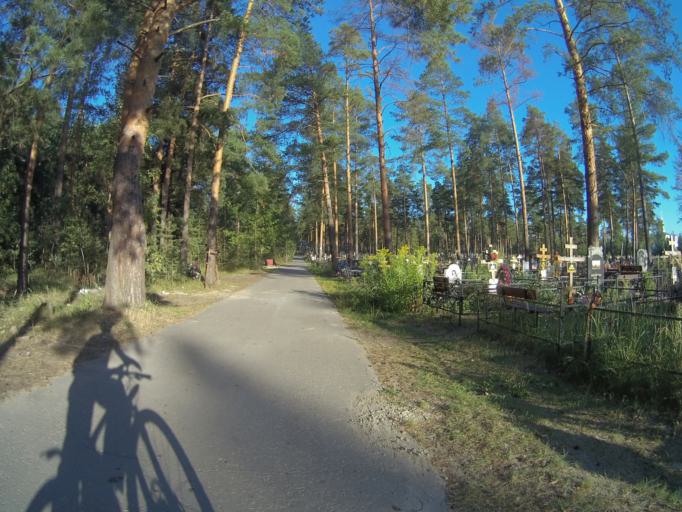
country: RU
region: Vladimir
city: Kommunar
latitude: 56.0455
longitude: 40.4368
